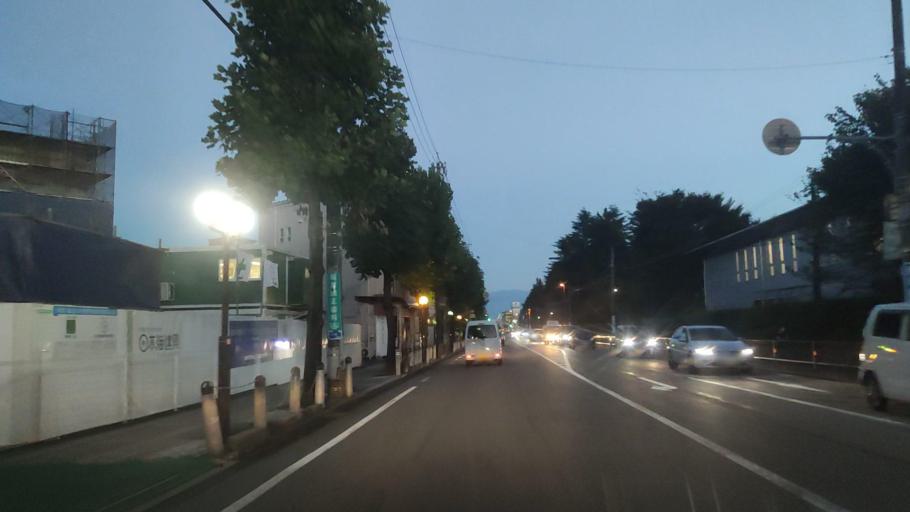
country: JP
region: Toyama
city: Toyama-shi
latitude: 36.7004
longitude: 137.1894
